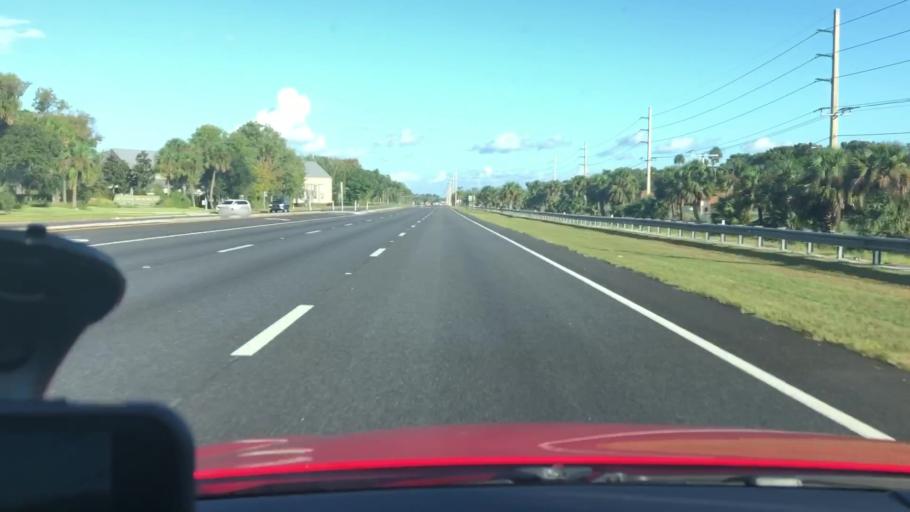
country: US
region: Florida
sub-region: Volusia County
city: Daytona Beach
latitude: 29.1951
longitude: -81.0350
